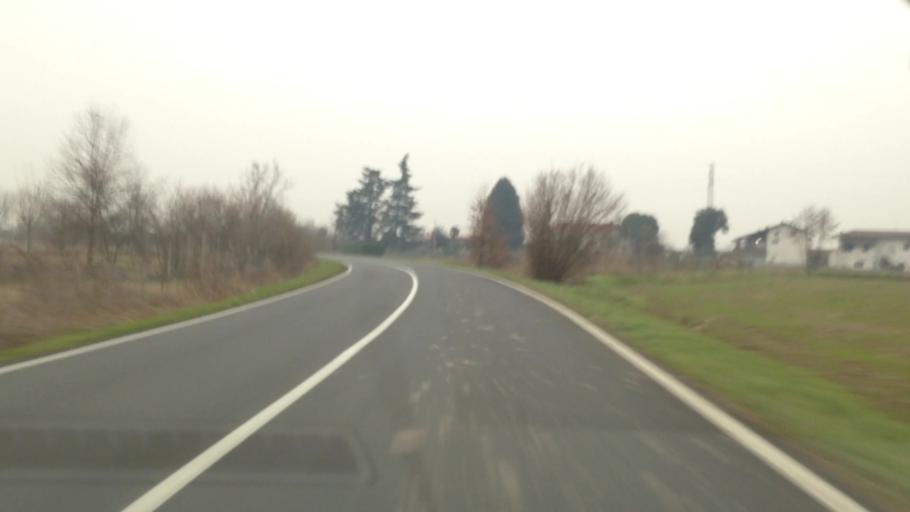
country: IT
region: Piedmont
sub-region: Provincia di Vercelli
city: Livorno Ferraris
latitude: 45.2844
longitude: 8.0627
